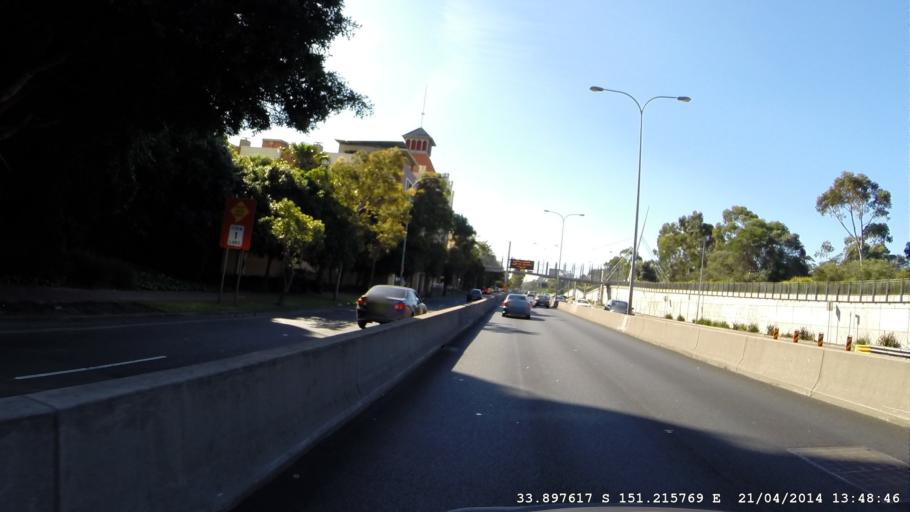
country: AU
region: New South Wales
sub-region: City of Sydney
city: Redfern
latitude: -33.8976
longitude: 151.2158
